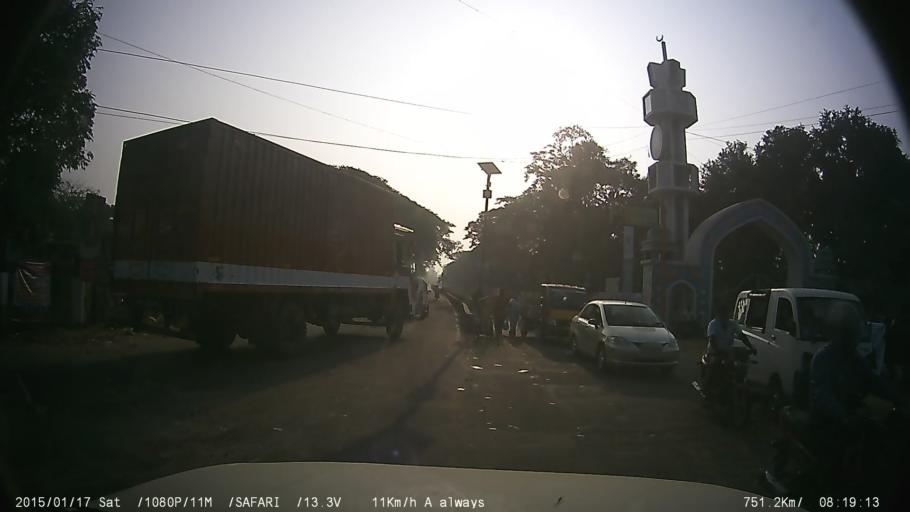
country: IN
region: Tamil Nadu
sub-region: Kancheepuram
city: Vandalur
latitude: 12.8791
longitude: 80.0800
